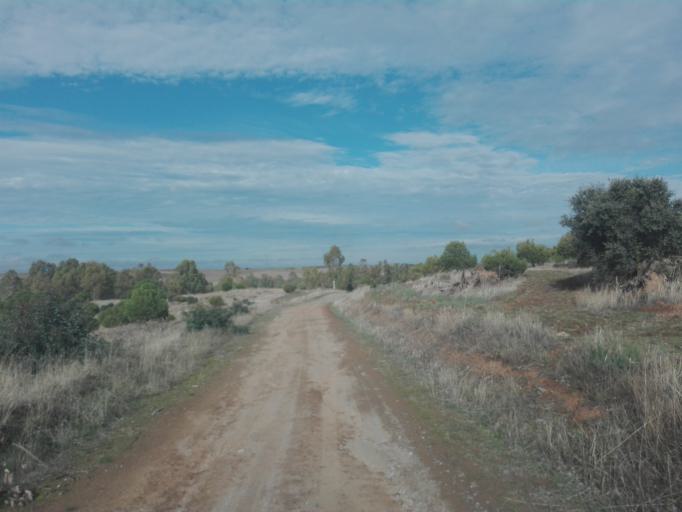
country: ES
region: Extremadura
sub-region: Provincia de Badajoz
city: Villagarcia de la Torre
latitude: 38.3223
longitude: -6.0870
